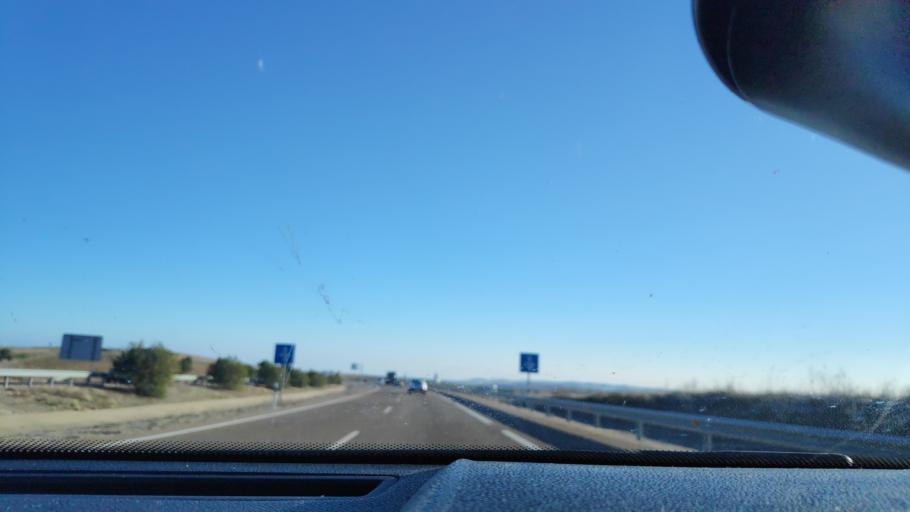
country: ES
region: Andalusia
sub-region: Provincia de Sevilla
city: Guillena
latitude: 37.5405
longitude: -6.0992
